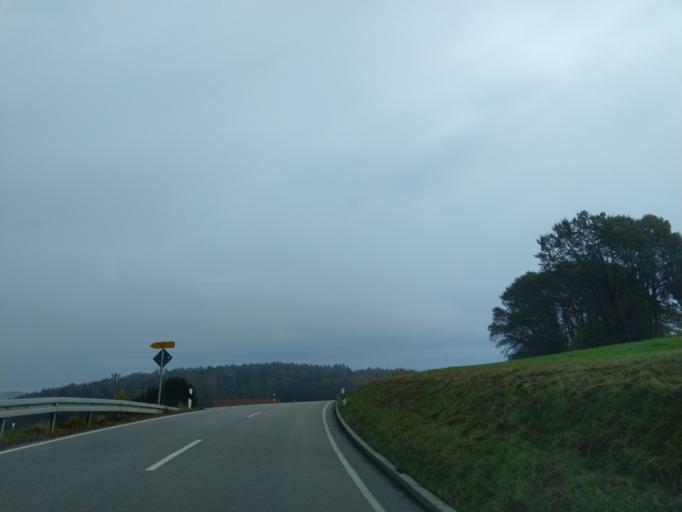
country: DE
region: Bavaria
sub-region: Lower Bavaria
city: Schollnach
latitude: 48.7769
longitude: 13.2016
